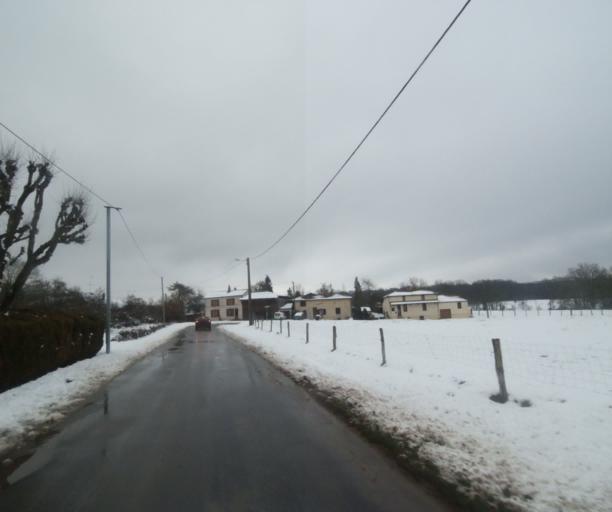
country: FR
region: Champagne-Ardenne
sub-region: Departement de la Haute-Marne
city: Laneuville-a-Remy
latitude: 48.4758
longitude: 4.8858
